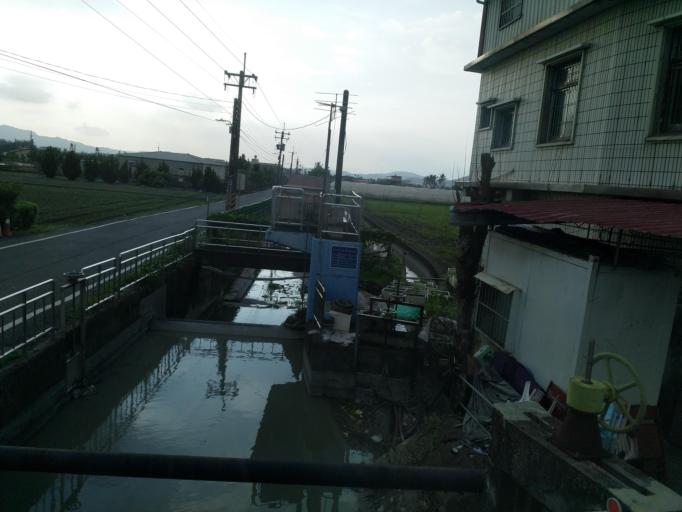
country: TW
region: Taiwan
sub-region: Pingtung
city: Pingtung
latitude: 22.8704
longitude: 120.5369
